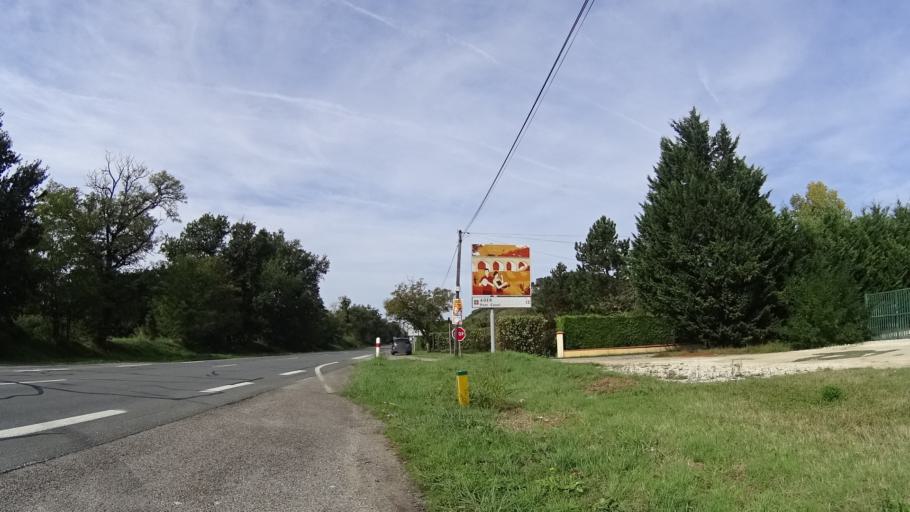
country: FR
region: Midi-Pyrenees
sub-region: Departement du Tarn-et-Garonne
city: Lamagistere
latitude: 44.1477
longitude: 0.7634
